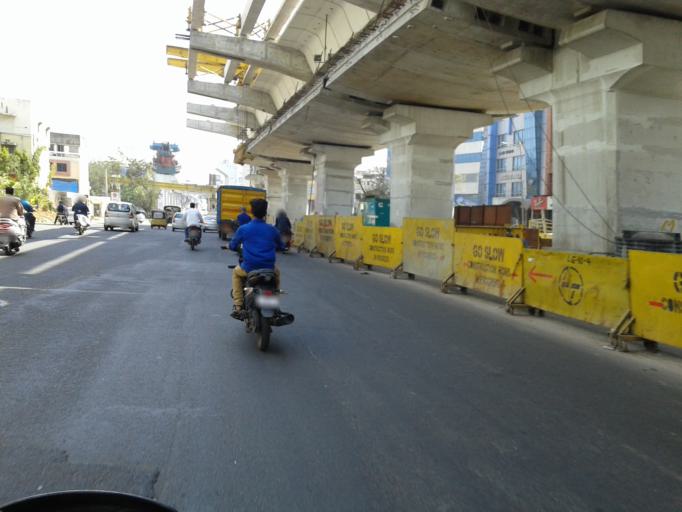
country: IN
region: Telangana
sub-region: Rangareddi
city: Quthbullapur
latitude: 17.4450
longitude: 78.4657
